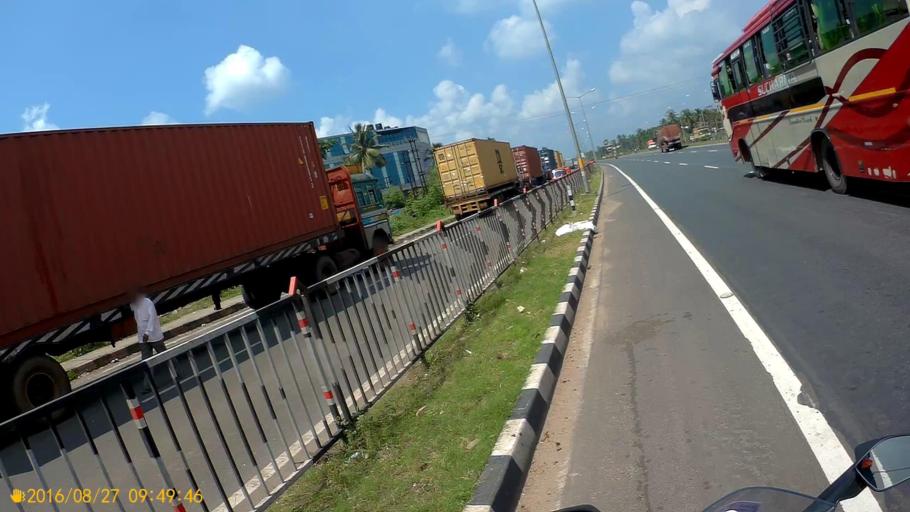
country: IN
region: West Bengal
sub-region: Haora
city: Dhulagari
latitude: 22.5737
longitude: 88.1769
